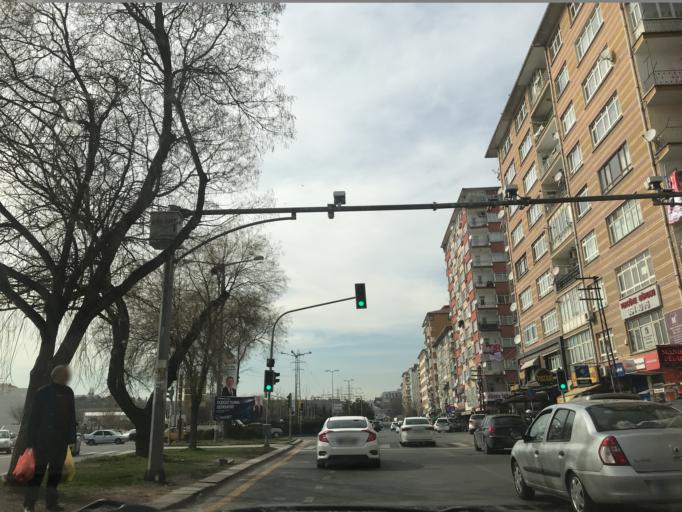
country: TR
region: Ankara
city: Batikent
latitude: 39.9580
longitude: 32.7911
